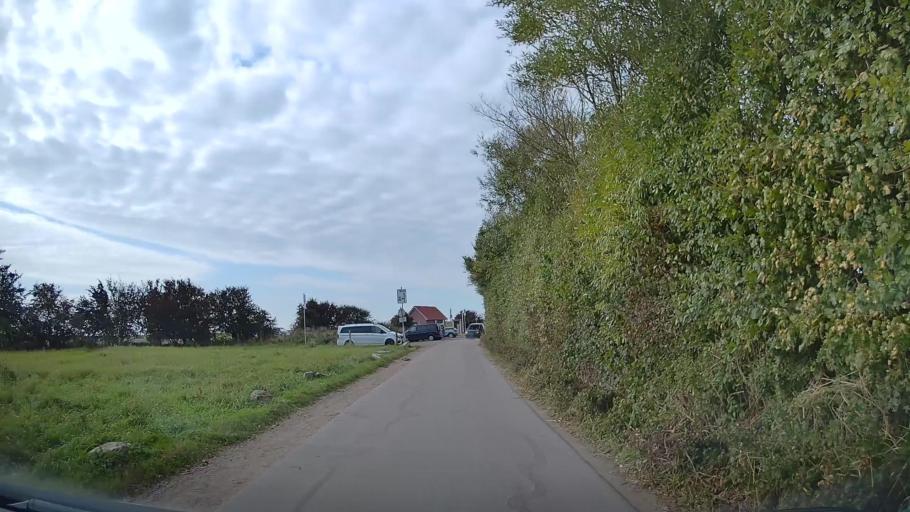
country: DE
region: Schleswig-Holstein
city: Grossenbrode
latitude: 54.5229
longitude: 11.0492
